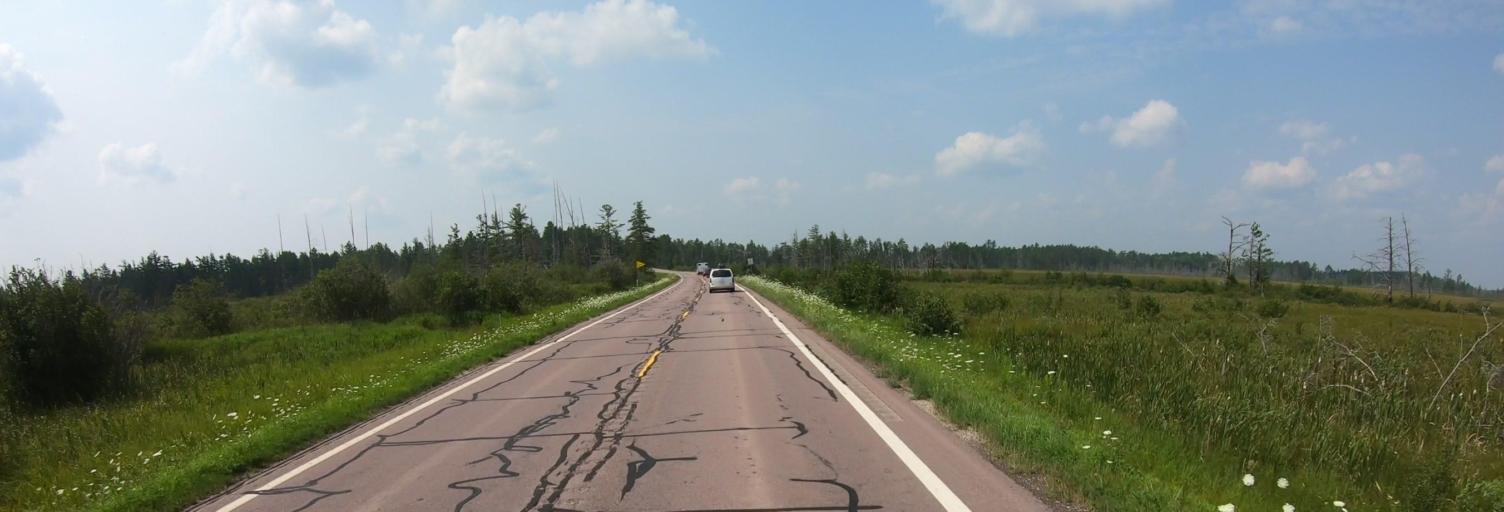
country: US
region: Michigan
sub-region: Luce County
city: Newberry
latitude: 46.4530
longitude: -85.4667
